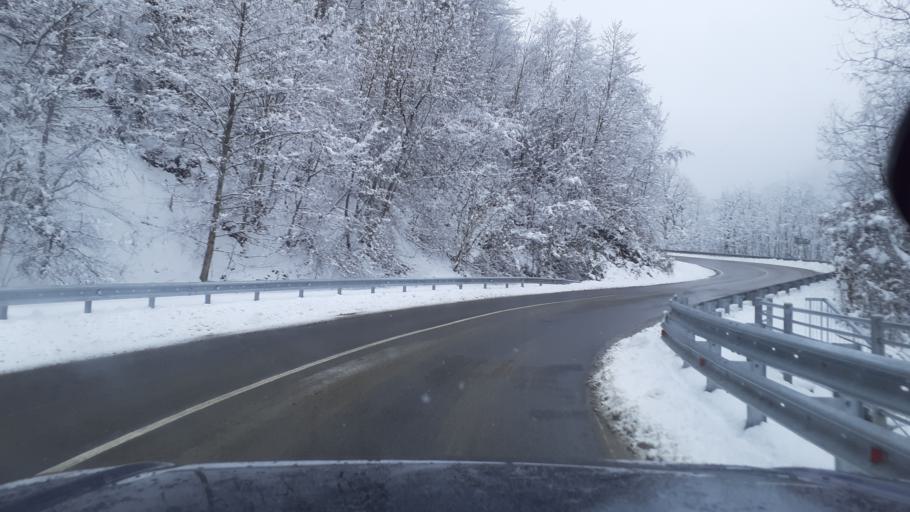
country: RU
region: Adygeya
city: Kamennomostskiy
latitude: 44.1806
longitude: 40.1567
